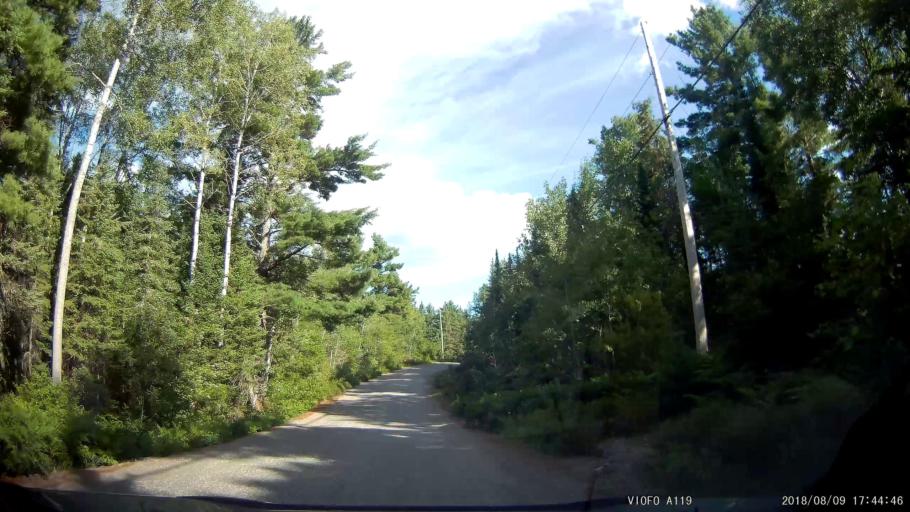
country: CA
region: Ontario
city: Rayside-Balfour
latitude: 46.6042
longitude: -81.5333
